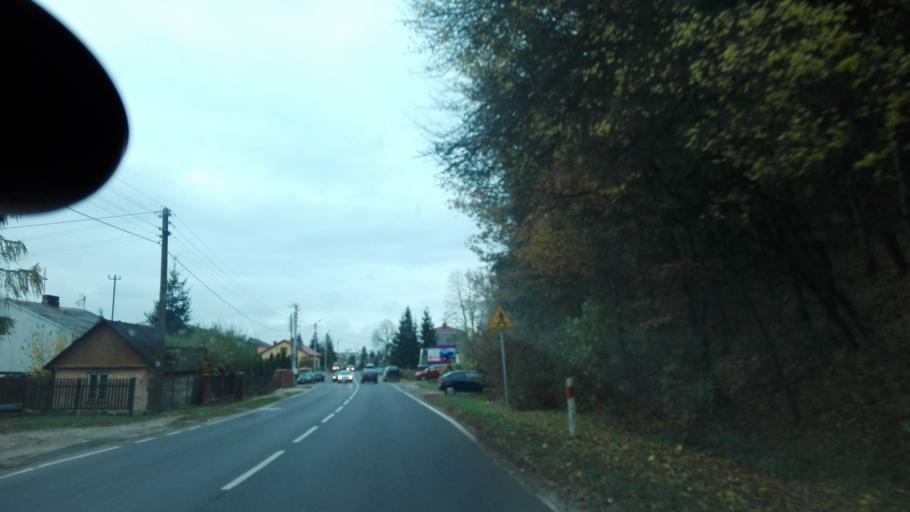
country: PL
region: Lublin Voivodeship
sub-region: Powiat pulawski
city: Pulawy
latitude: 51.4180
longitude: 21.9269
